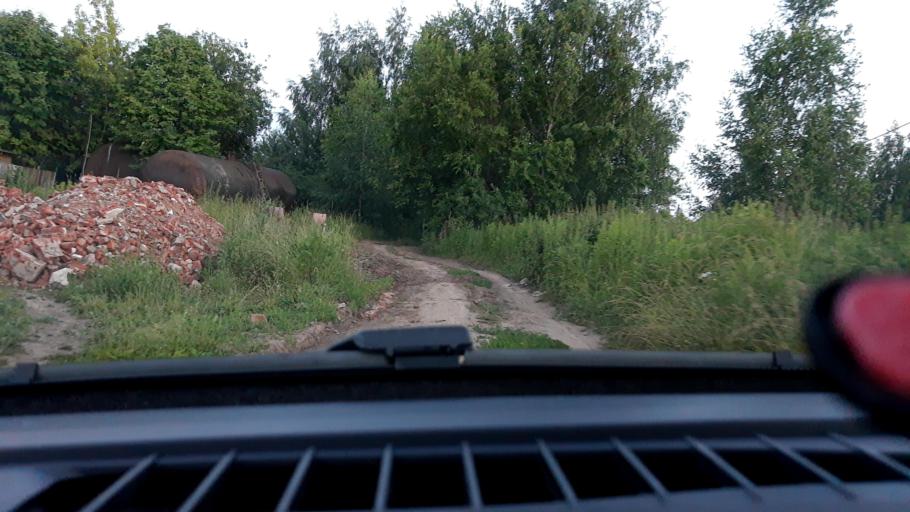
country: RU
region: Nizjnij Novgorod
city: Afonino
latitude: 56.2503
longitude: 44.0646
